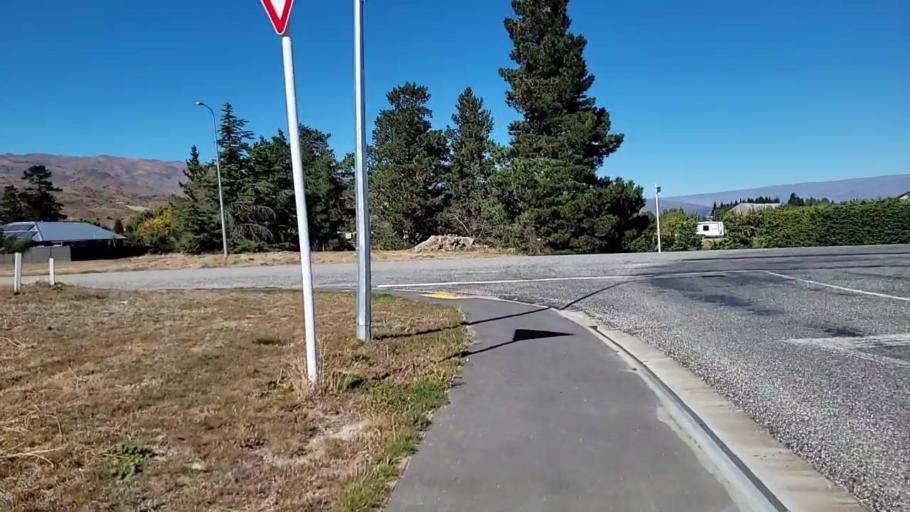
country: NZ
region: Otago
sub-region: Queenstown-Lakes District
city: Wanaka
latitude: -44.9774
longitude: 169.2375
